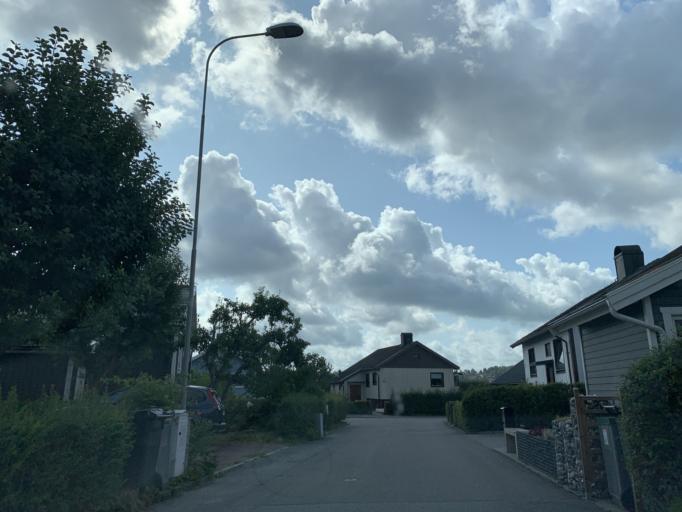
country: SE
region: Vaestra Goetaland
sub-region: Partille Kommun
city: Partille
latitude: 57.7400
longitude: 12.0673
